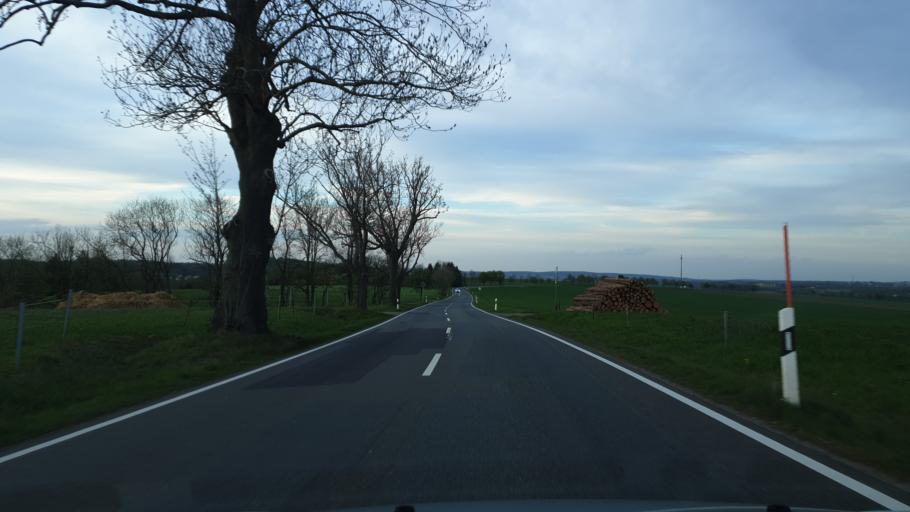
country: DE
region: Saxony
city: Oelsnitz
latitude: 50.7042
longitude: 12.6869
